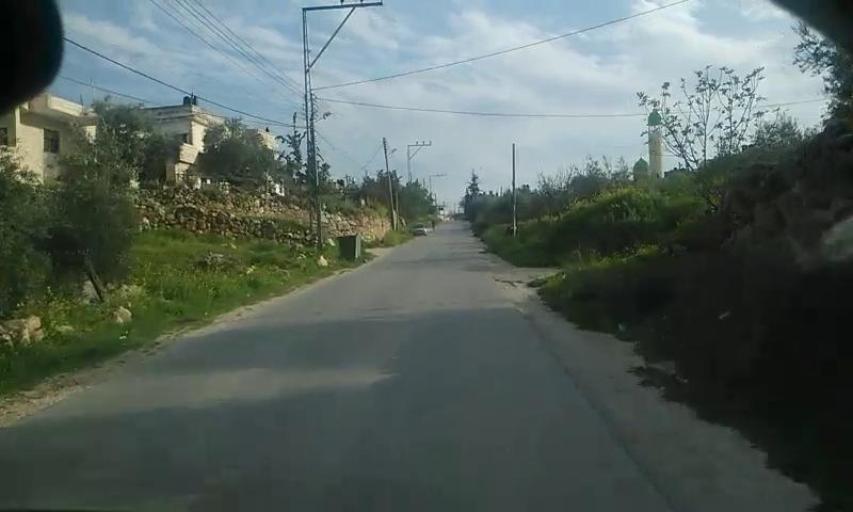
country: PS
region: West Bank
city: Nuba
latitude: 31.6122
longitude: 35.0342
